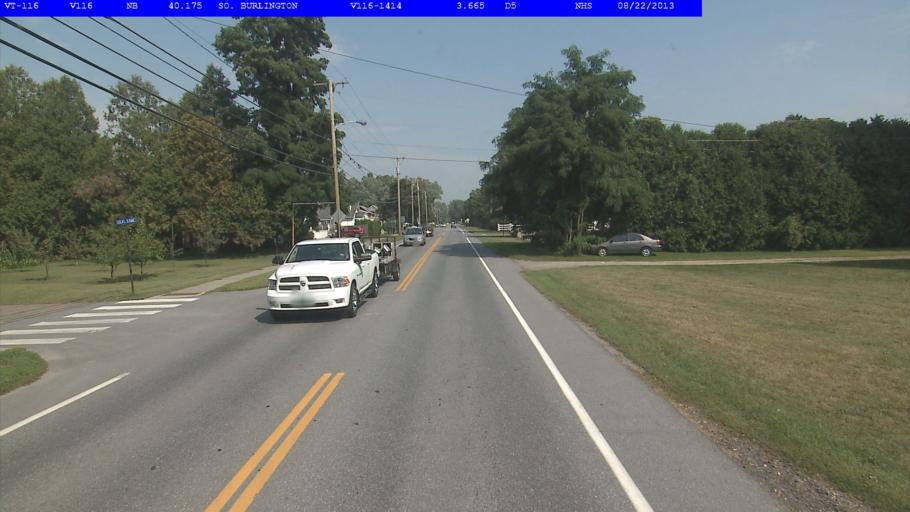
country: US
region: Vermont
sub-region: Chittenden County
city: South Burlington
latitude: 44.4588
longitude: -73.1698
